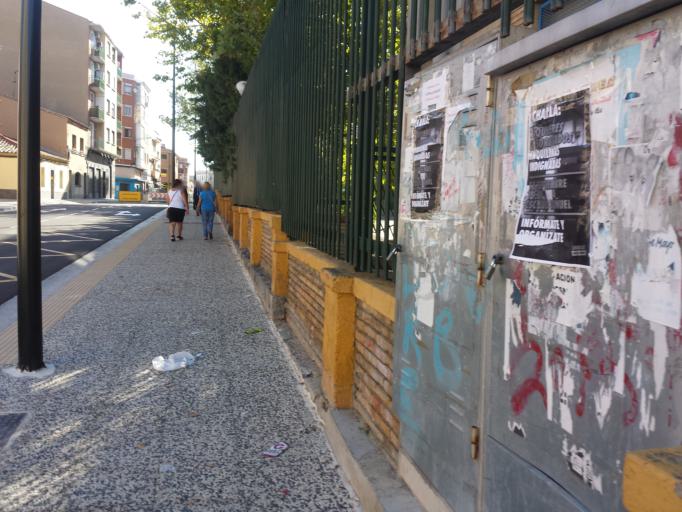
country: ES
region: Aragon
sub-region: Provincia de Zaragoza
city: Oliver-Valdefierro, Oliver, Valdefierro
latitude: 41.6516
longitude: -0.9277
